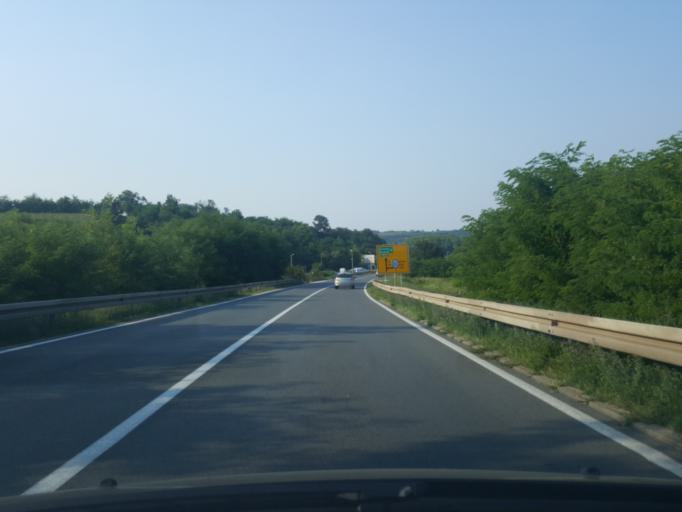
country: RS
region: Central Serbia
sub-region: Belgrade
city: Sopot
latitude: 44.5581
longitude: 20.6674
